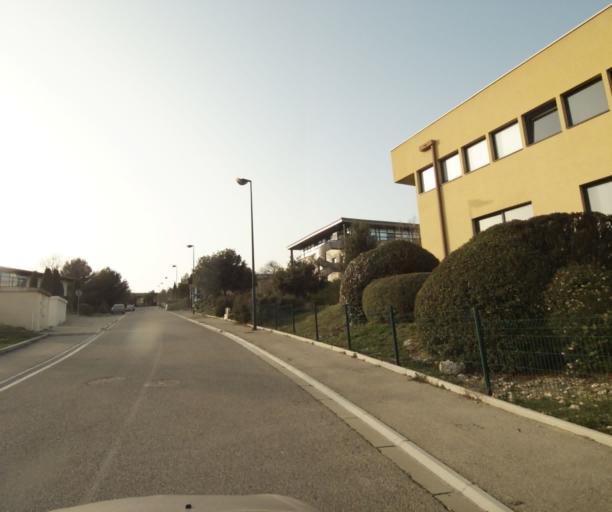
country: FR
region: Provence-Alpes-Cote d'Azur
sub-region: Departement des Bouches-du-Rhone
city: Cabries
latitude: 43.4932
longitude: 5.3464
